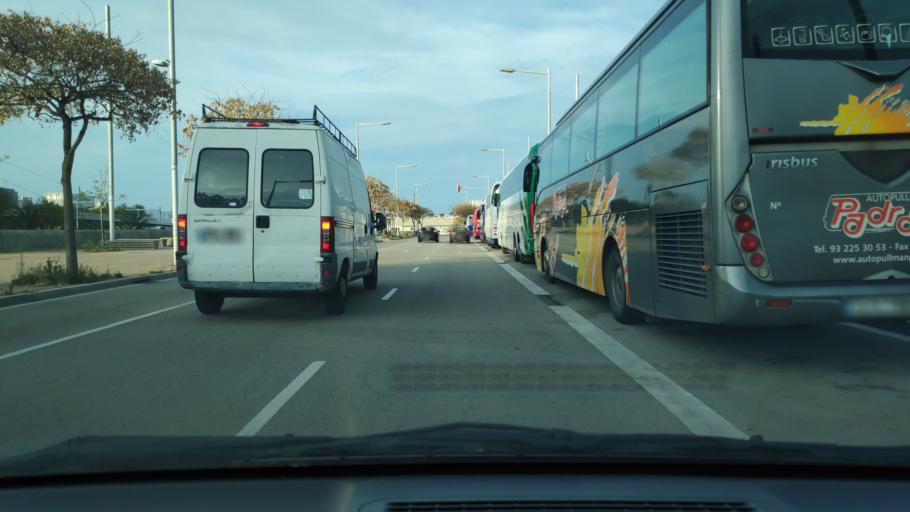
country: ES
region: Catalonia
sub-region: Provincia de Barcelona
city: Sant Marti
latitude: 41.4065
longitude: 2.2196
